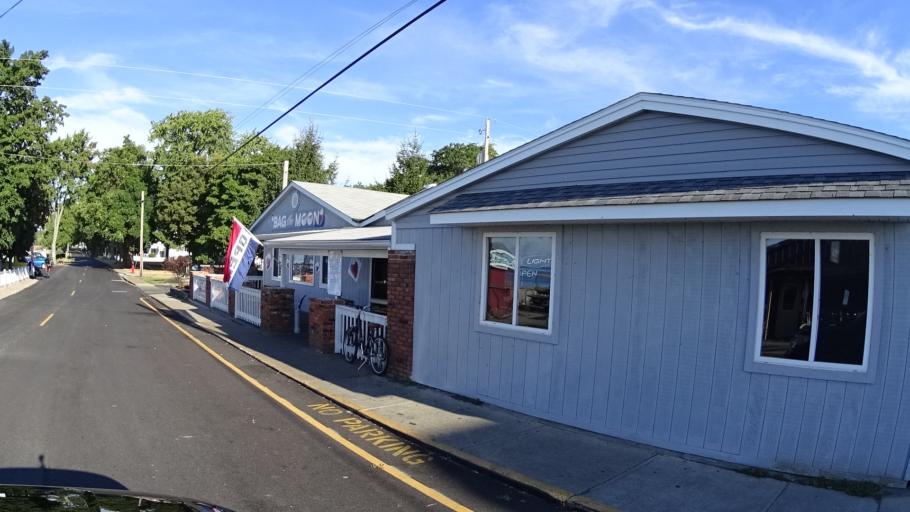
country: US
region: Ohio
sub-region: Erie County
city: Sandusky
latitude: 41.5941
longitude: -82.7117
